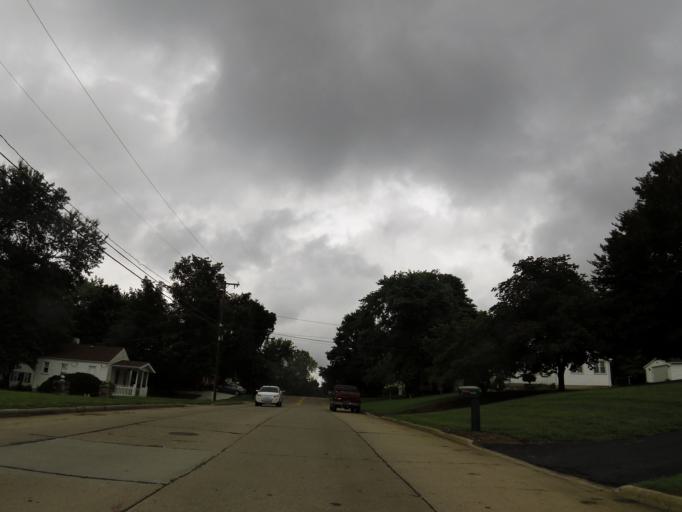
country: US
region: Missouri
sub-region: Cape Girardeau County
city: Cape Girardeau
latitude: 37.3195
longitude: -89.5464
